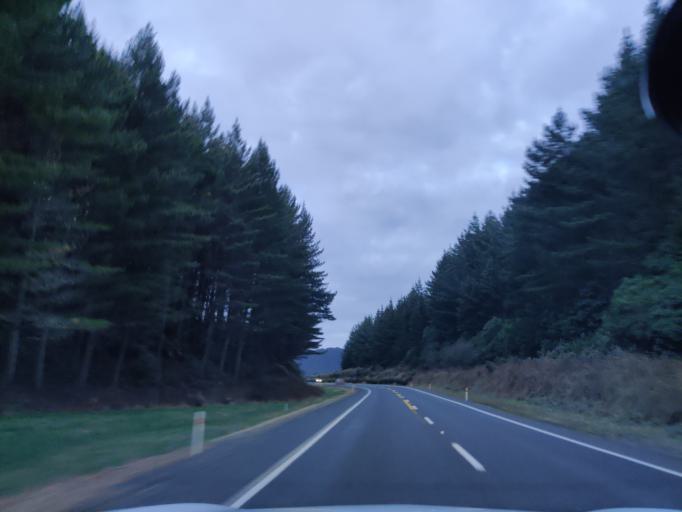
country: NZ
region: Waikato
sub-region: South Waikato District
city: Tokoroa
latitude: -38.4162
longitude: 176.0518
